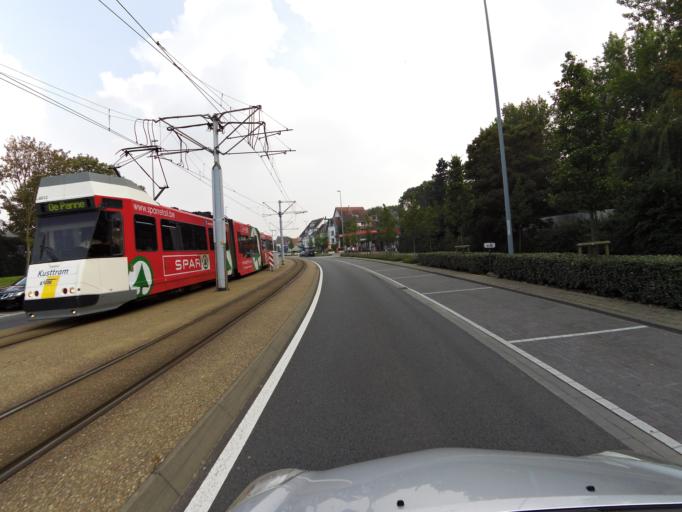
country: BE
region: Flanders
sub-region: Provincie West-Vlaanderen
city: Nieuwpoort
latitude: 51.1342
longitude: 2.7439
